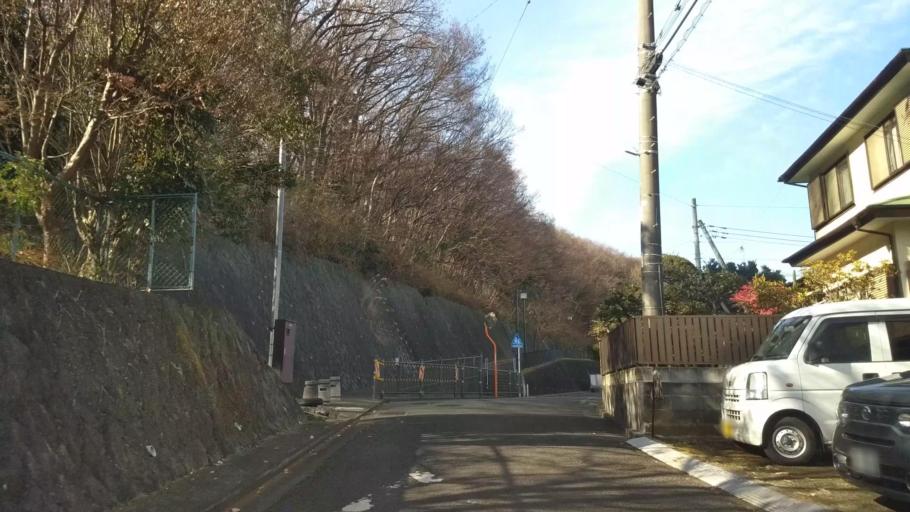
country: JP
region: Kanagawa
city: Hadano
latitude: 35.3577
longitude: 139.2283
